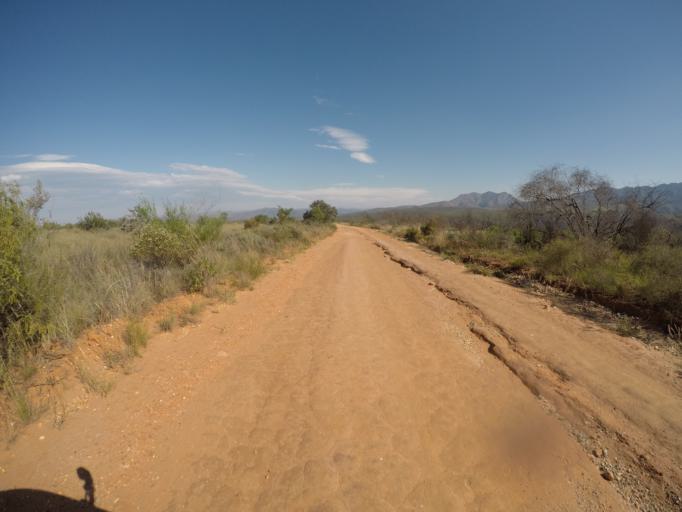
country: ZA
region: Eastern Cape
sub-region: Cacadu District Municipality
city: Kareedouw
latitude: -33.6363
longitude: 24.4593
